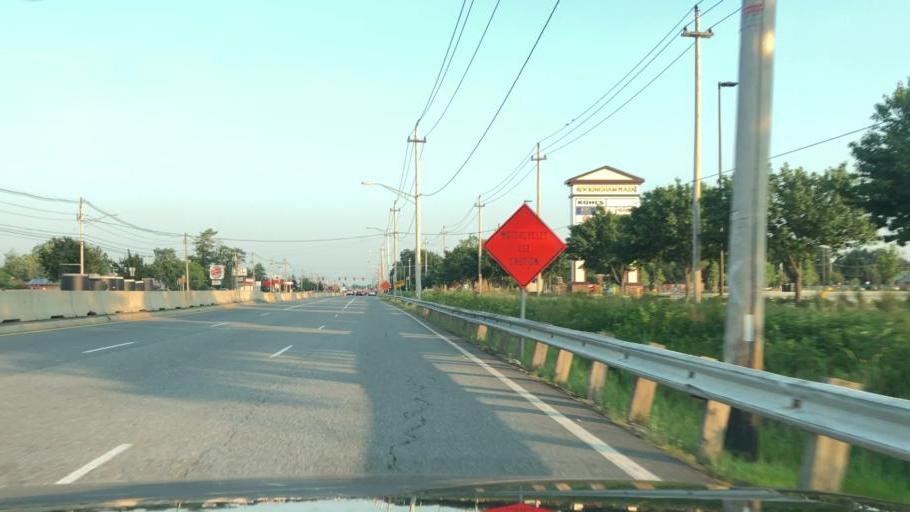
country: US
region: New Hampshire
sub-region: Rockingham County
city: Salem
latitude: 42.7679
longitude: -71.2196
